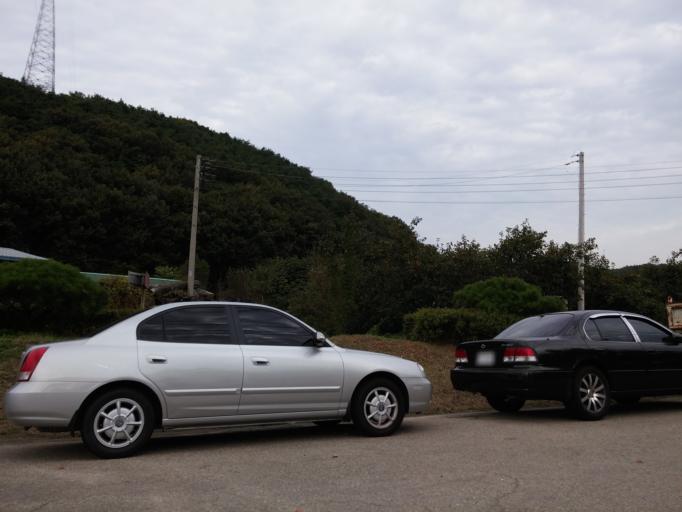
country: KR
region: Chungcheongnam-do
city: Yonmu
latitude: 36.1549
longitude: 127.2074
